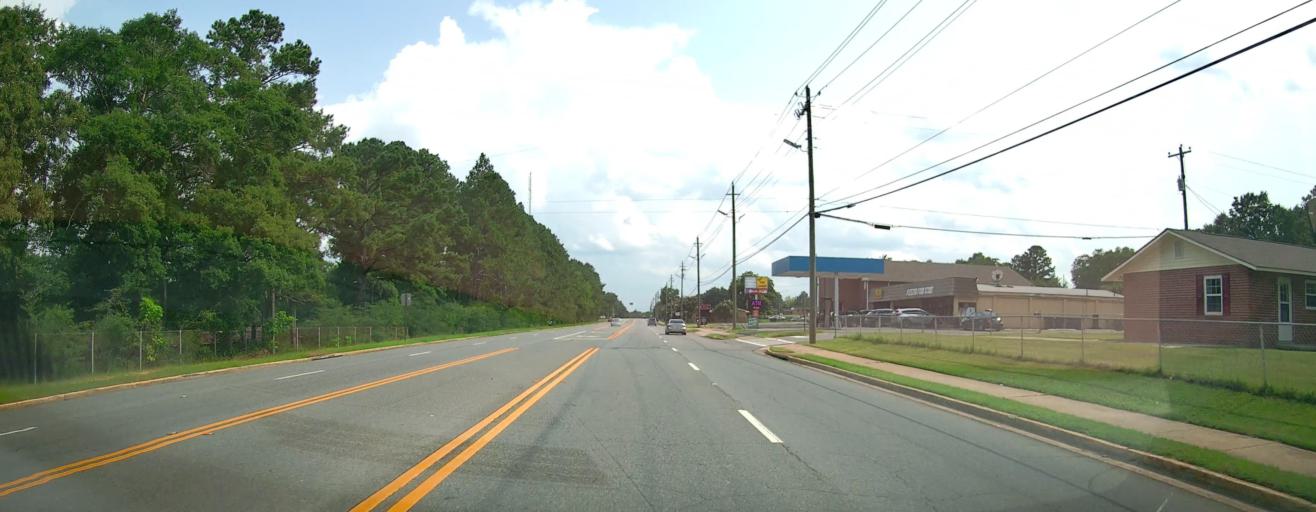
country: US
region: Georgia
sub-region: Houston County
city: Warner Robins
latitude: 32.6068
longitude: -83.6131
